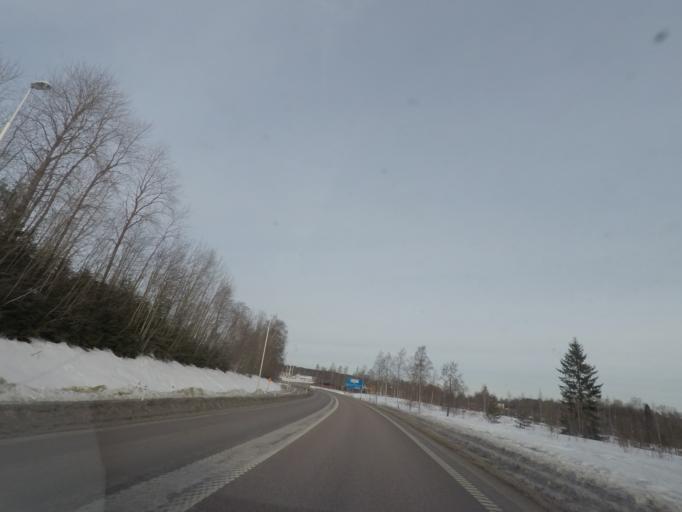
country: SE
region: Vaestmanland
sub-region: Fagersta Kommun
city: Fagersta
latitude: 59.9812
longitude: 15.8145
